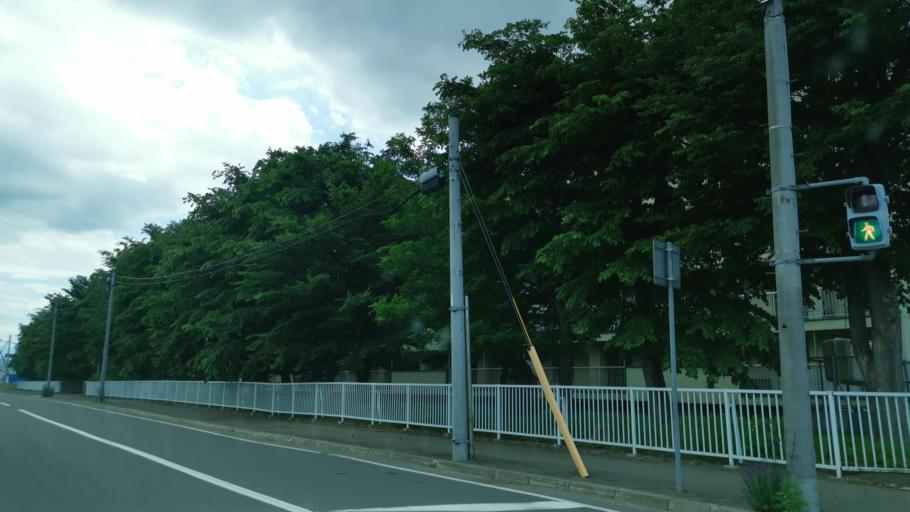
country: JP
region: Hokkaido
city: Sapporo
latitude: 43.0744
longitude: 141.3928
